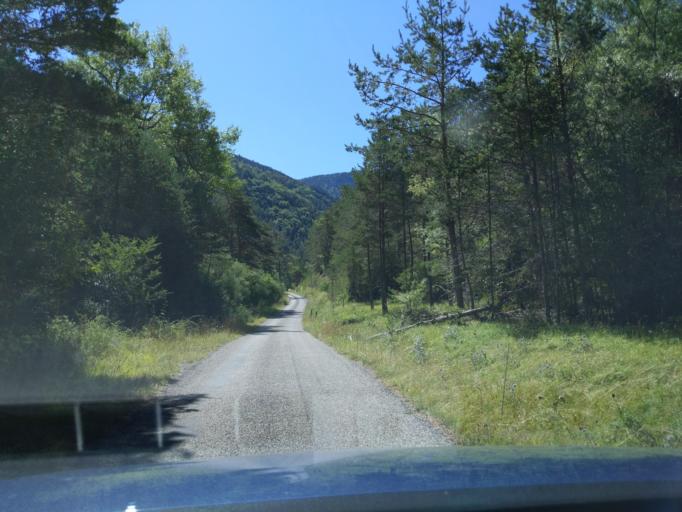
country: FR
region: Rhone-Alpes
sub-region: Departement de la Drome
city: Die
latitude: 44.6321
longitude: 5.5535
